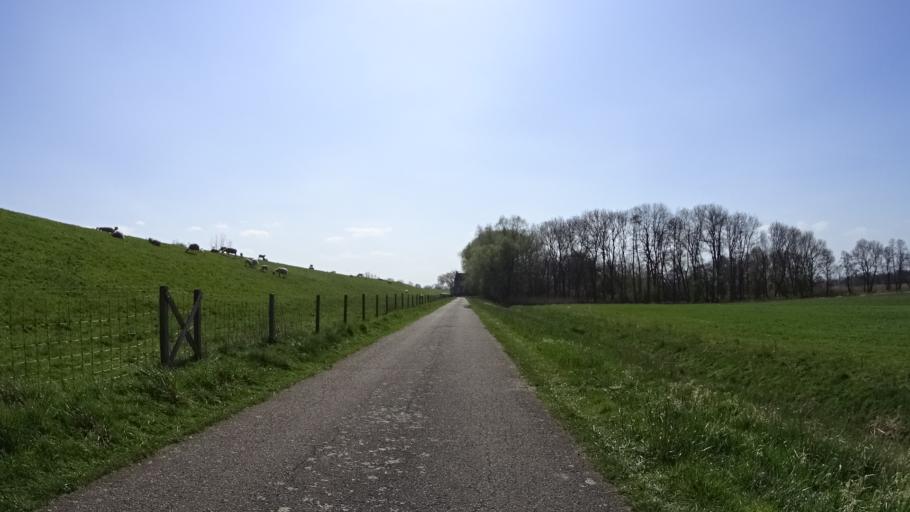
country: DE
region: Lower Saxony
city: Weener
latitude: 53.1192
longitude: 7.3718
